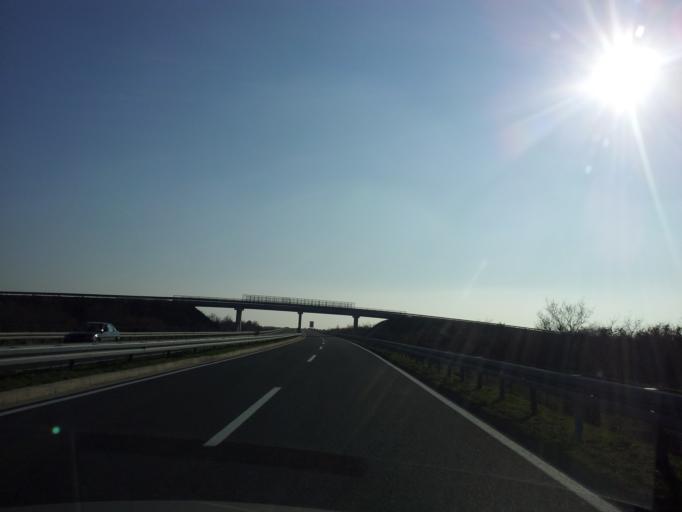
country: HR
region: Zadarska
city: Galovac
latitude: 44.0841
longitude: 15.3546
